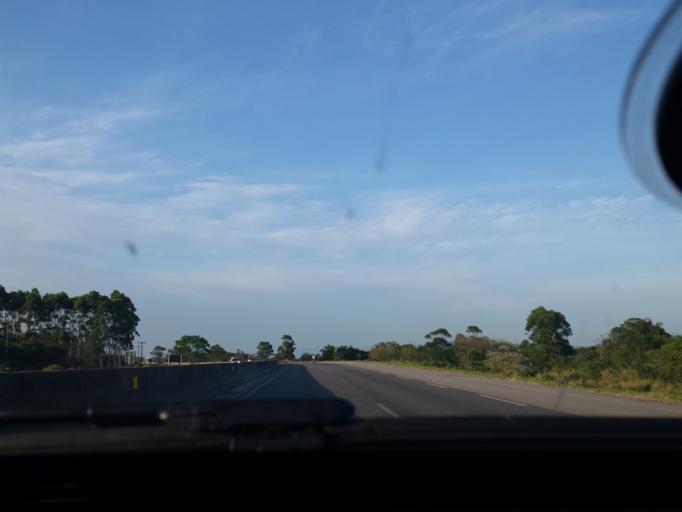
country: BR
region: Santa Catarina
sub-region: Imbituba
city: Imbituba
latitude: -28.3005
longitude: -48.7184
